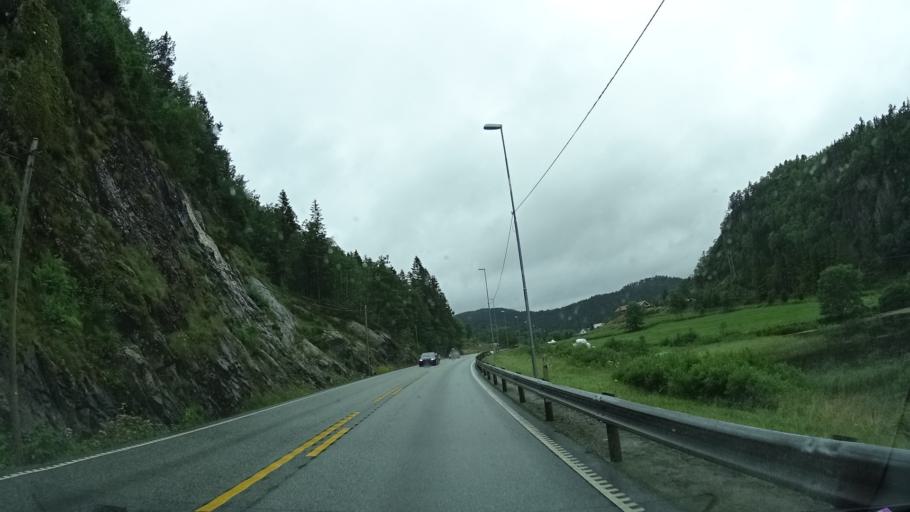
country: NO
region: Vest-Agder
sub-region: Flekkefjord
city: Flekkefjord
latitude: 58.3647
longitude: 6.6354
